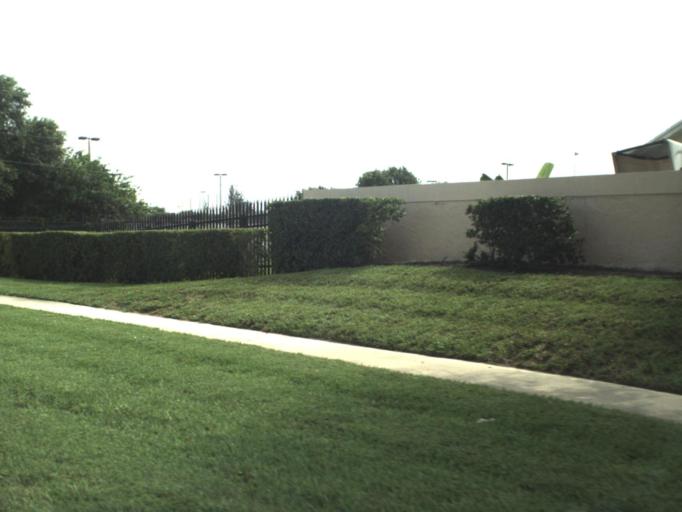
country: US
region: Florida
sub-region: Palm Beach County
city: Mangonia Park
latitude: 26.7787
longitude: -80.0874
